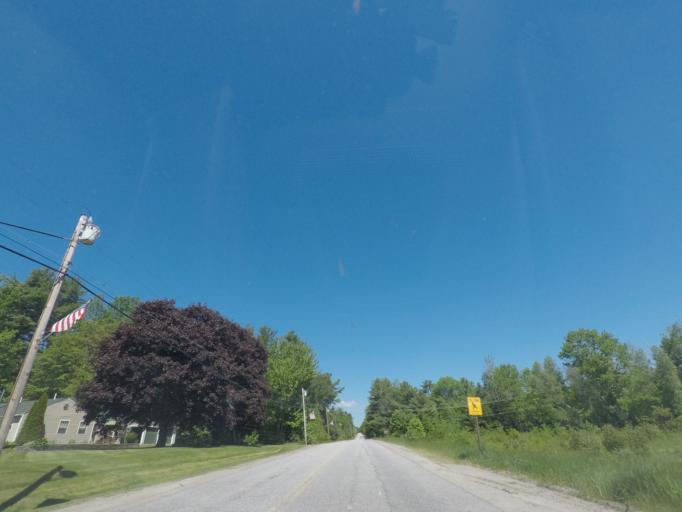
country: US
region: Maine
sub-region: Kennebec County
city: Manchester
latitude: 44.2281
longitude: -69.8774
